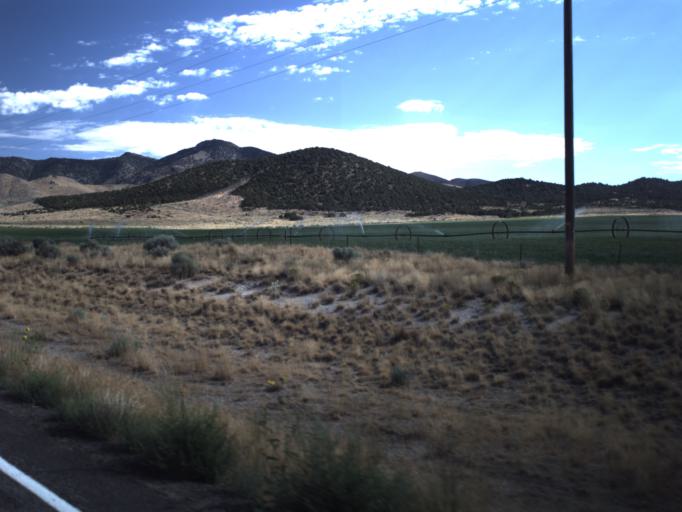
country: US
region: Utah
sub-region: Juab County
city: Mona
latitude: 39.8844
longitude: -112.1380
